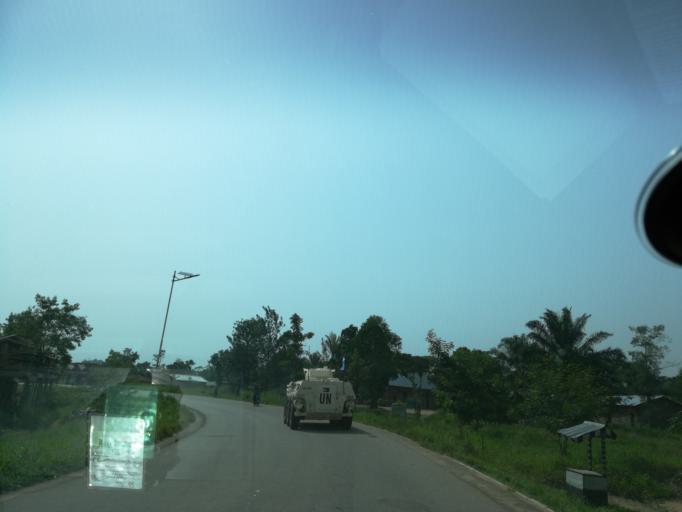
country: CD
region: Nord Kivu
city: Beni
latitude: 0.5398
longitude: 29.4906
